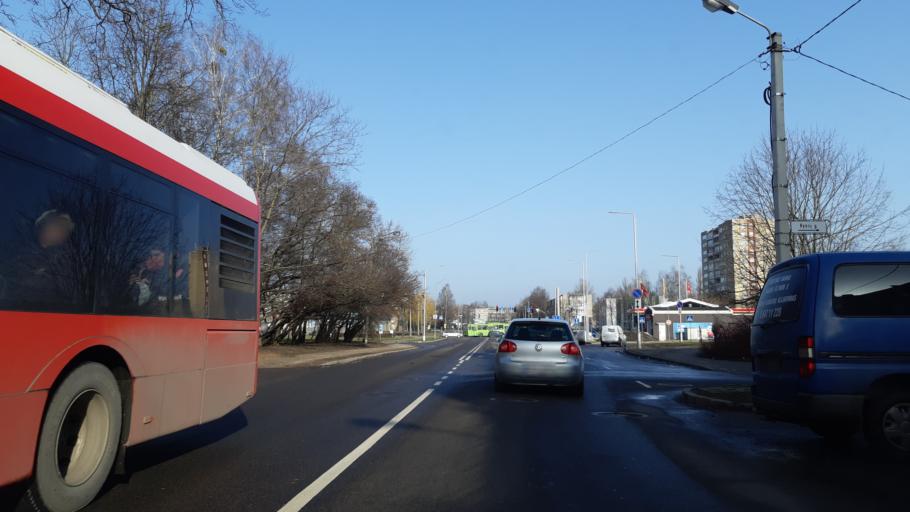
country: LT
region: Kauno apskritis
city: Dainava (Kaunas)
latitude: 54.9108
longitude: 23.9560
